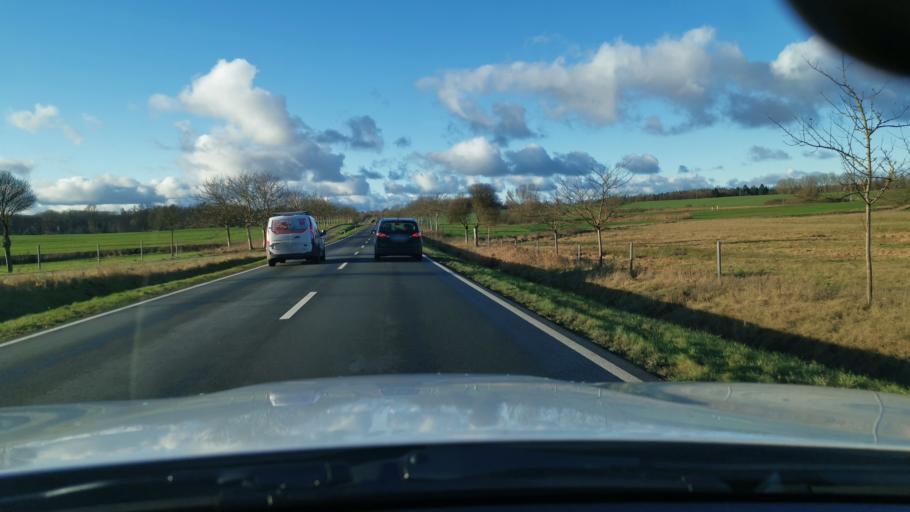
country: DE
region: Mecklenburg-Vorpommern
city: Tessin
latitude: 54.0377
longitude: 12.4268
